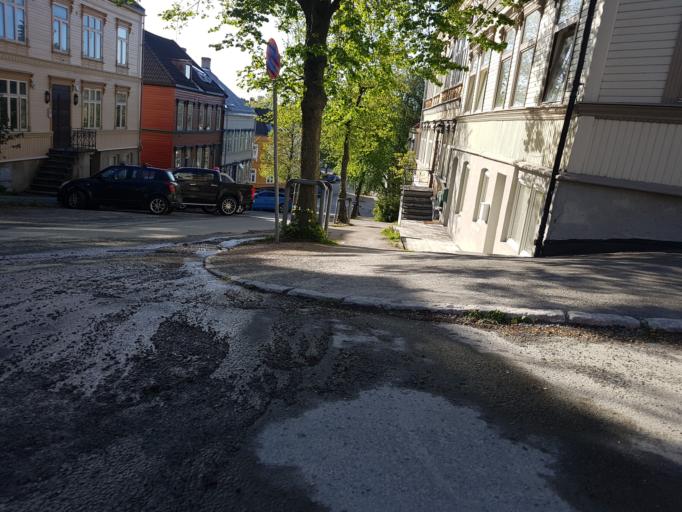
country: NO
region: Sor-Trondelag
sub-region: Trondheim
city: Trondheim
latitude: 63.4338
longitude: 10.4188
